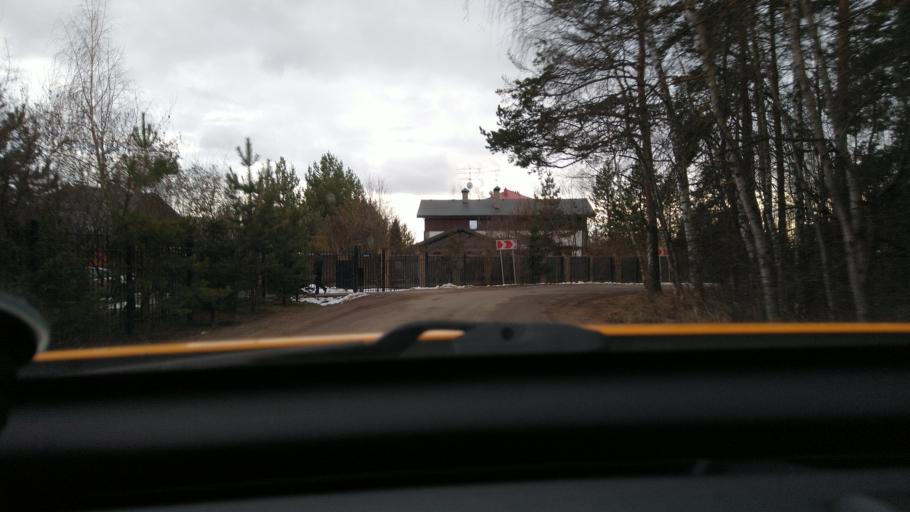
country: RU
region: Moskovskaya
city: Petrovo-Dal'neye
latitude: 55.7608
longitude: 37.2052
